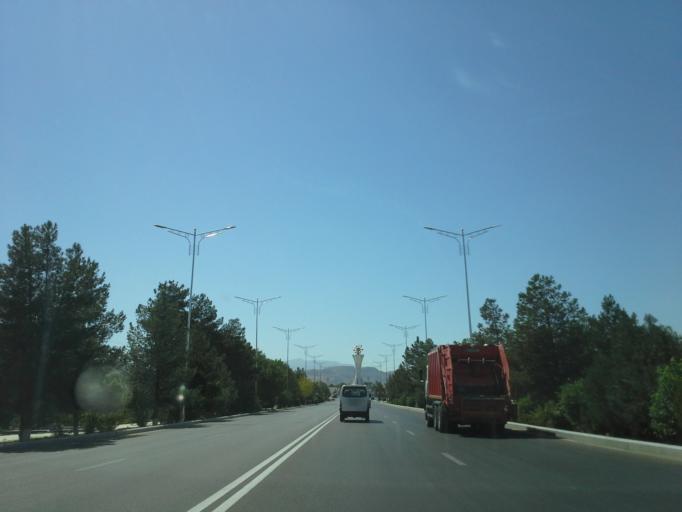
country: TM
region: Ahal
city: Ashgabat
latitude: 37.9303
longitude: 58.2985
